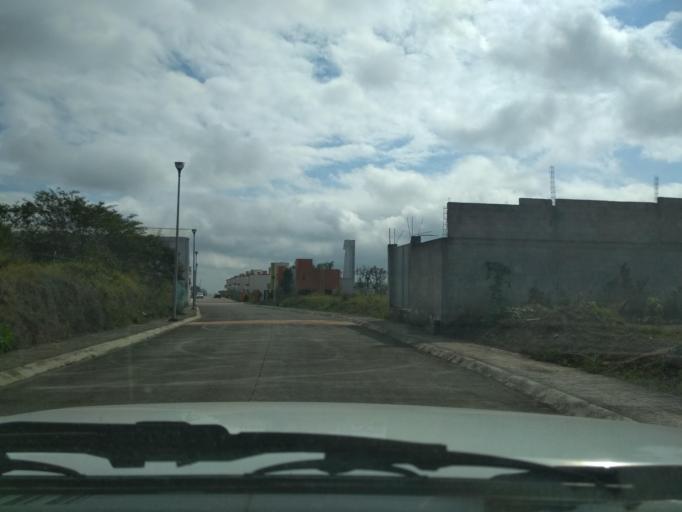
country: MX
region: Veracruz
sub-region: Emiliano Zapata
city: Jacarandas
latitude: 19.4990
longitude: -96.8413
